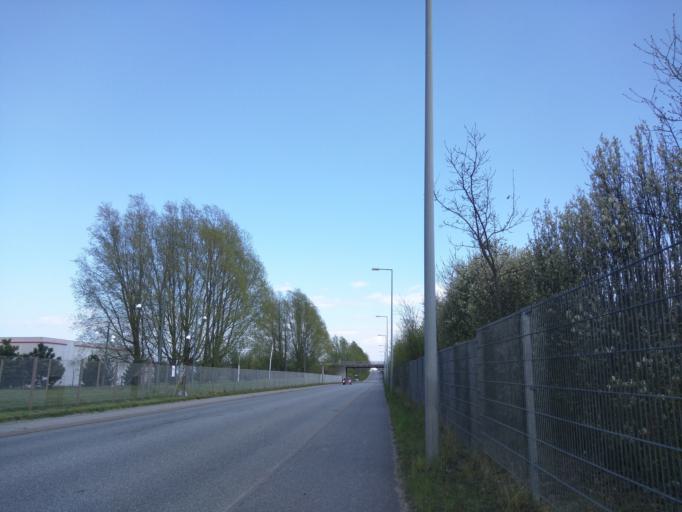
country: DK
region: South Denmark
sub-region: Fredericia Kommune
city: Snoghoj
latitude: 55.5409
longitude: 9.6981
